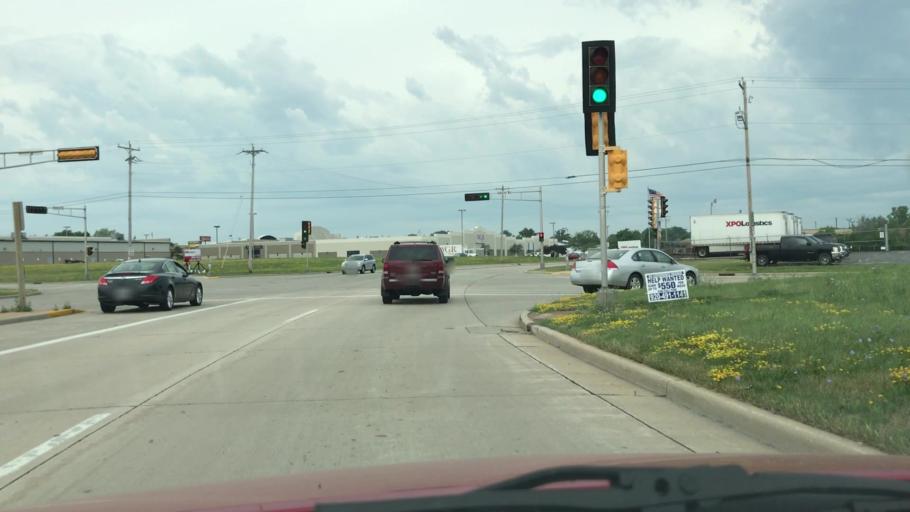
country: US
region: Wisconsin
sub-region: Brown County
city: Ashwaubenon
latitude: 44.4760
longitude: -88.0685
